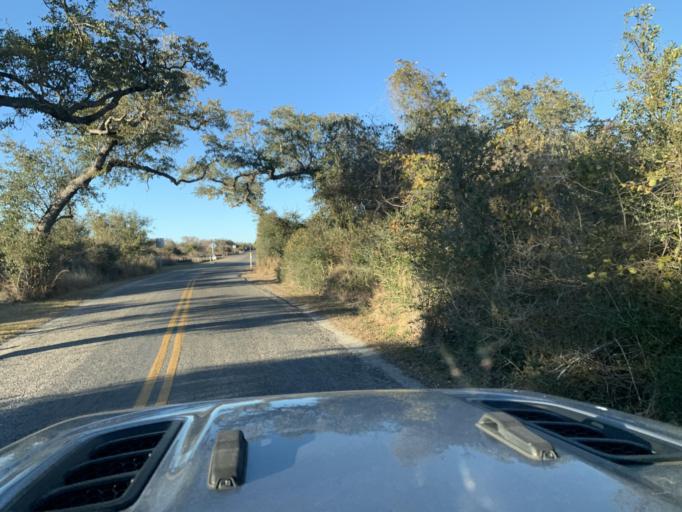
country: US
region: Texas
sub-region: Aransas County
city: Fulton
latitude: 28.1342
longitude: -96.9843
